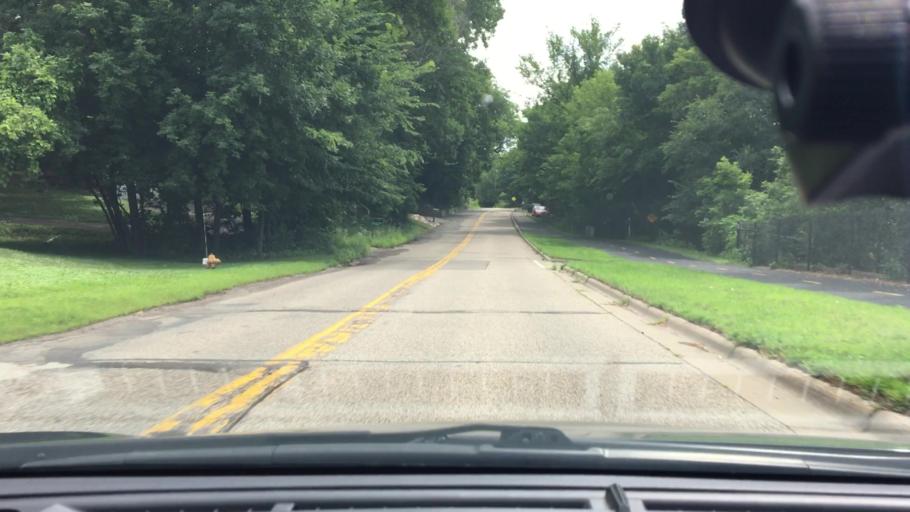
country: US
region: Minnesota
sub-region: Hennepin County
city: New Hope
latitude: 45.0144
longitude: -93.4168
